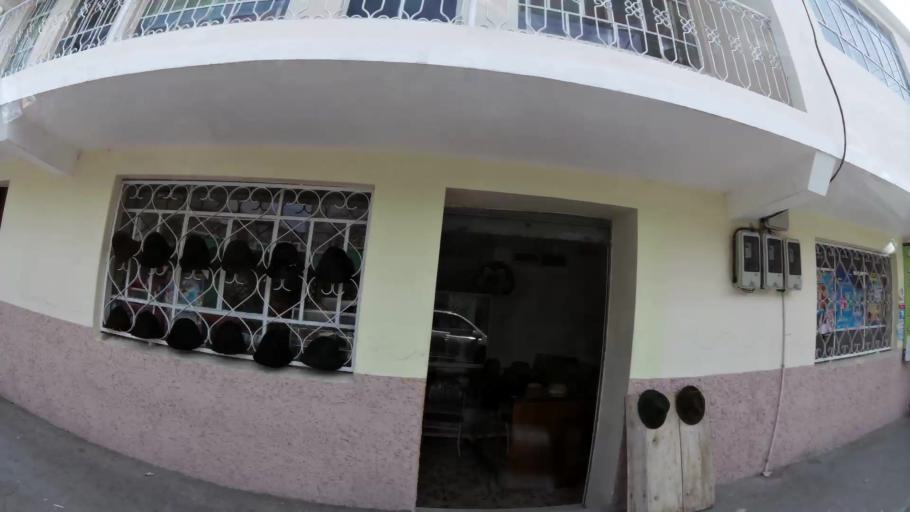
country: EC
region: Cotopaxi
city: San Miguel de Salcedo
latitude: -1.0444
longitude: -78.5872
